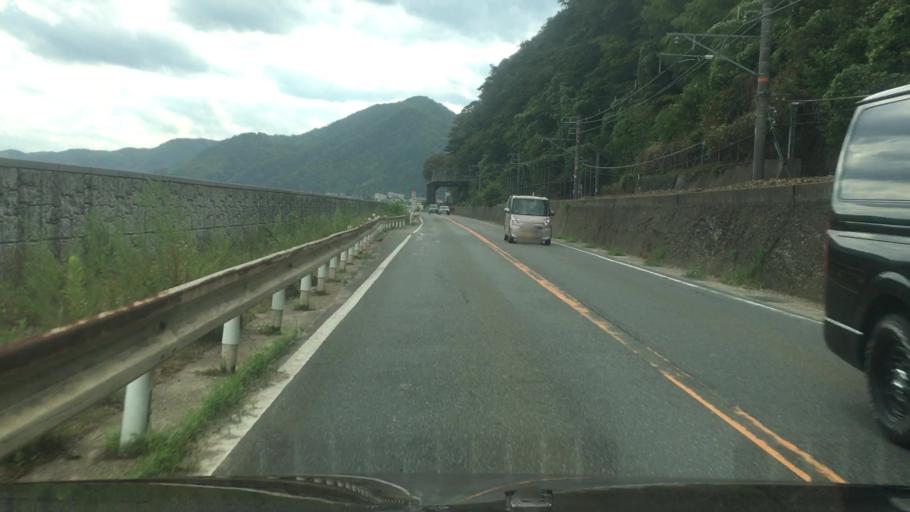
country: JP
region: Hyogo
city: Toyooka
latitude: 35.6131
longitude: 134.8072
